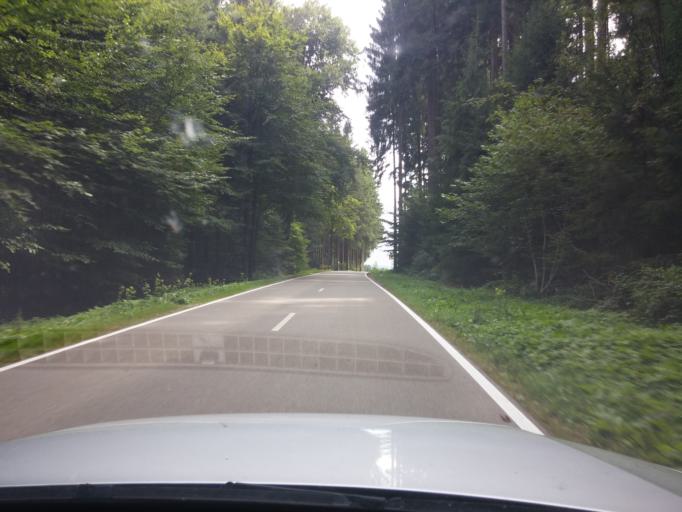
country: DE
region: Baden-Wuerttemberg
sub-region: Tuebingen Region
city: Aichstetten
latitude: 47.8505
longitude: 10.0833
